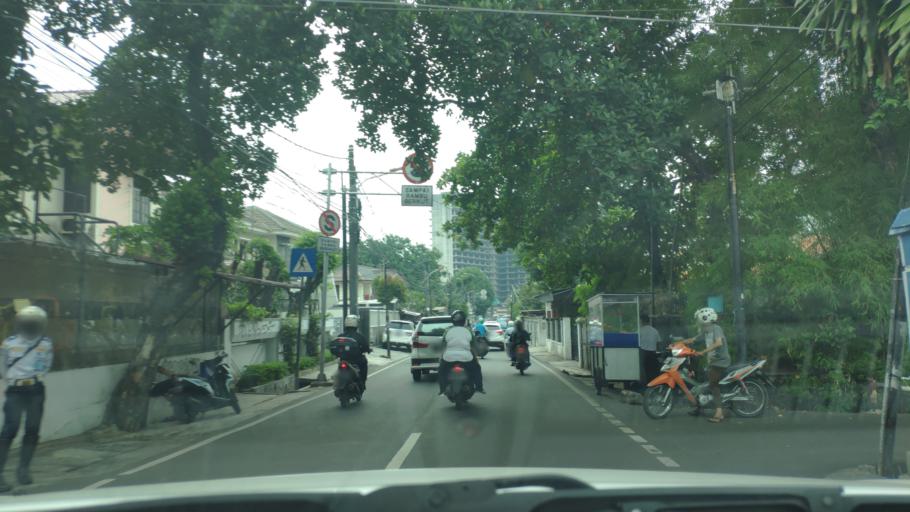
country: ID
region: Jakarta Raya
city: Jakarta
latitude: -6.1931
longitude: 106.7846
